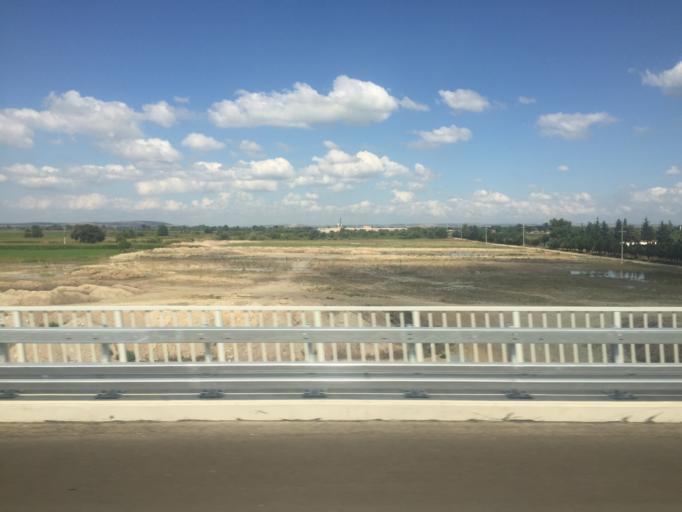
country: TR
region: Balikesir
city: Gobel
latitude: 40.0687
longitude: 28.2490
